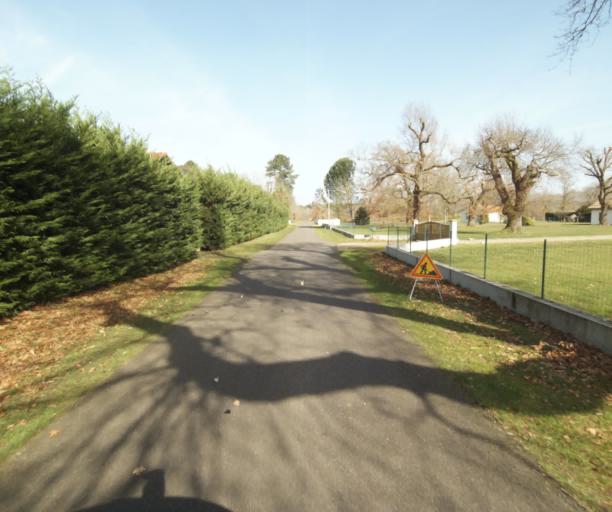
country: FR
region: Aquitaine
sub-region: Departement des Landes
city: Roquefort
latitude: 44.1324
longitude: -0.2496
